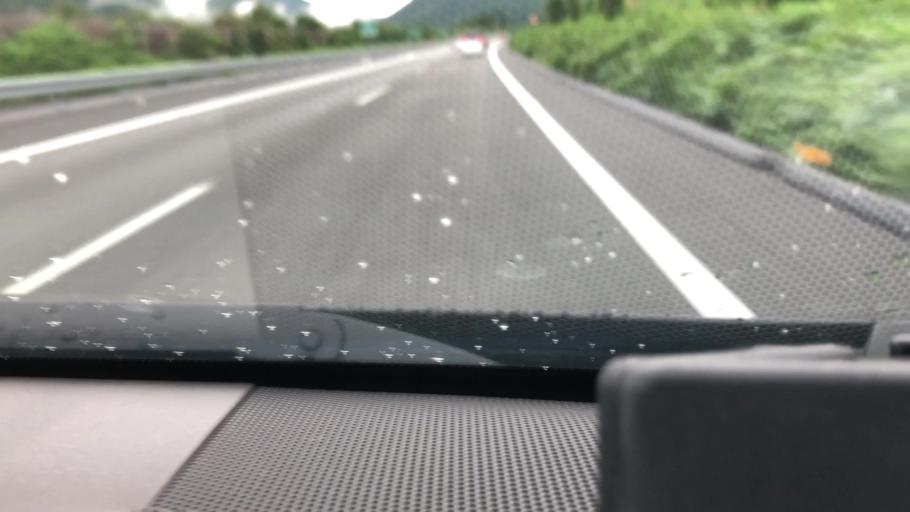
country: JP
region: Shizuoka
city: Mori
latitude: 34.8428
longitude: 137.9943
